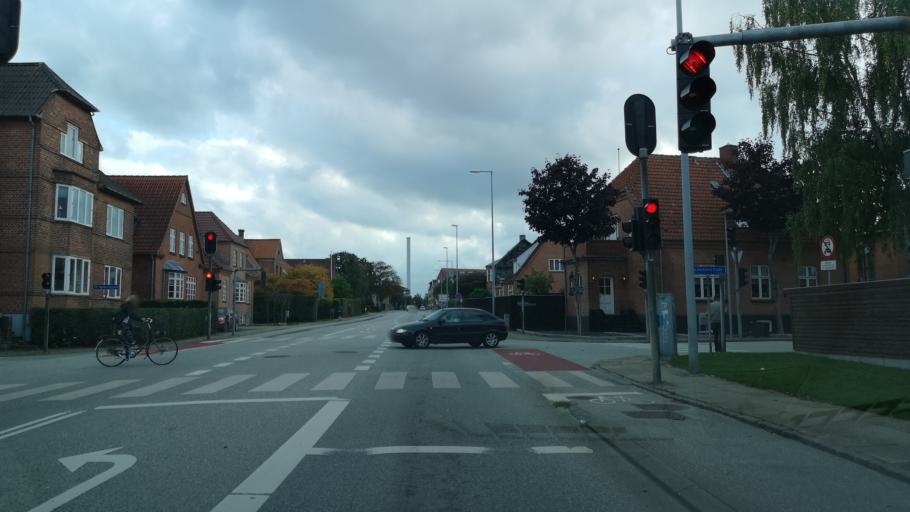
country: DK
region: Central Jutland
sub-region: Herning Kommune
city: Herning
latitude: 56.1370
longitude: 8.9871
